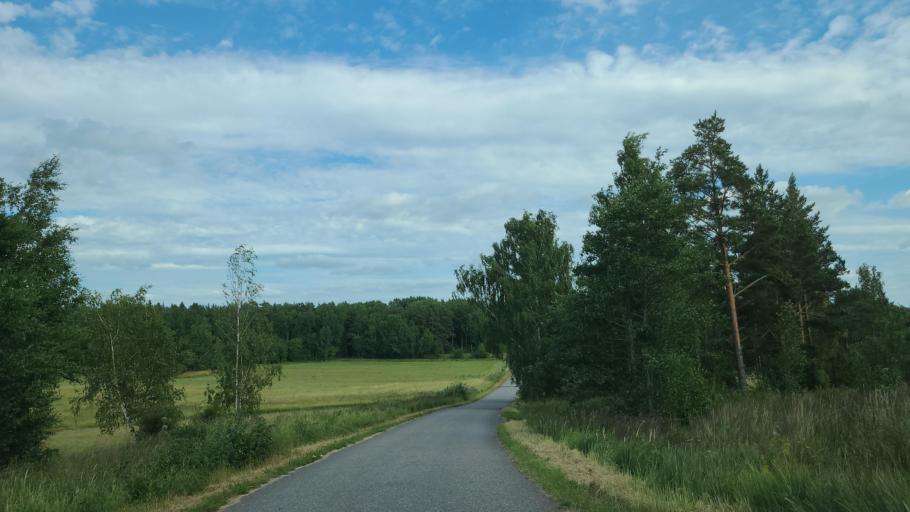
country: FI
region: Varsinais-Suomi
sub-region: Turku
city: Rymaettylae
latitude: 60.2900
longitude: 21.9605
